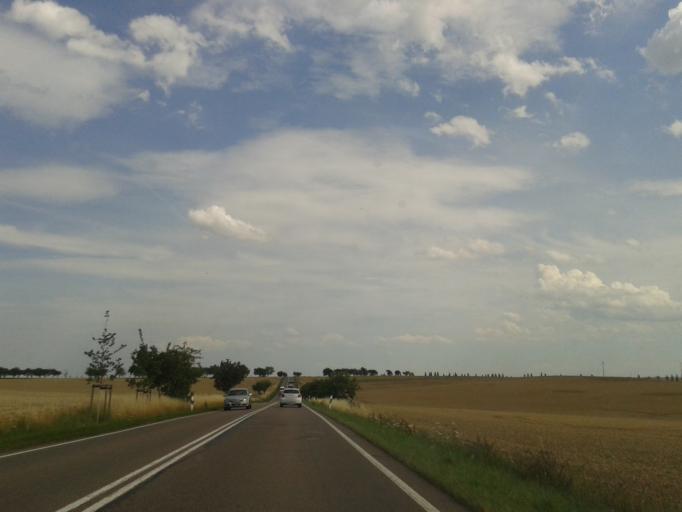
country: DE
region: Saxony
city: Wilsdruff
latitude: 51.0446
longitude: 13.5621
